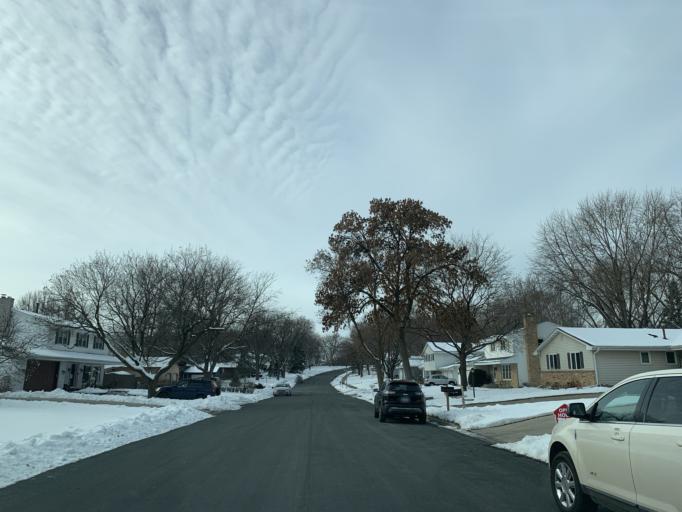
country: US
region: Minnesota
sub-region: Scott County
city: Savage
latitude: 44.8202
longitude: -93.3401
